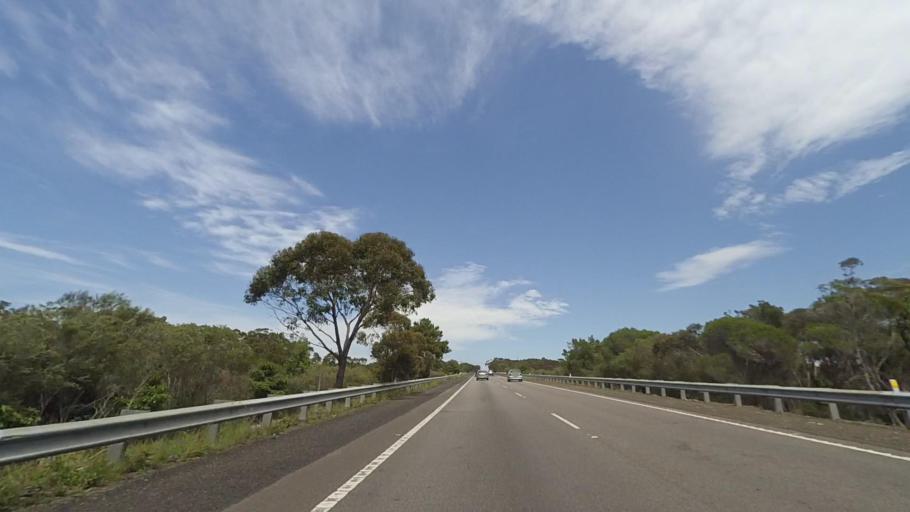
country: AU
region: New South Wales
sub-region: Wollongong
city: Bulli
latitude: -34.2958
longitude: 150.9178
